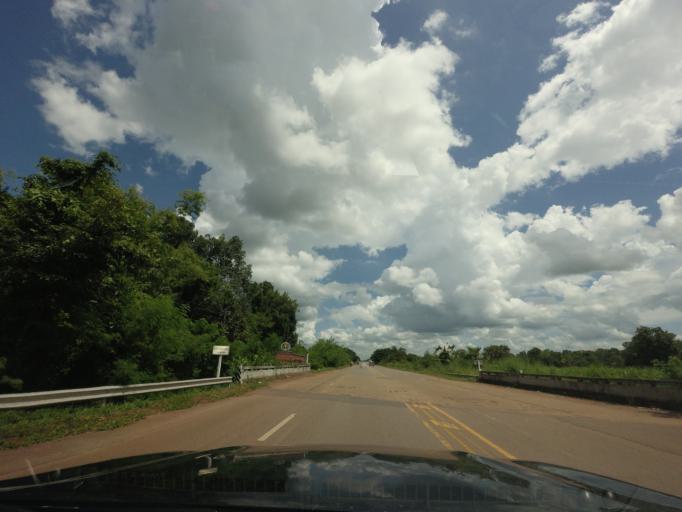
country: TH
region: Changwat Udon Thani
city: Ban Dung
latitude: 17.6807
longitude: 103.2300
